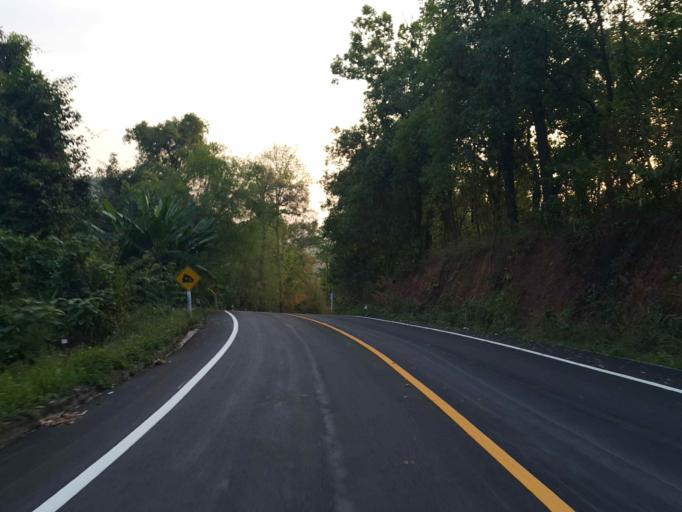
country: TH
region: Chiang Mai
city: Mae On
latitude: 19.0064
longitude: 99.3172
